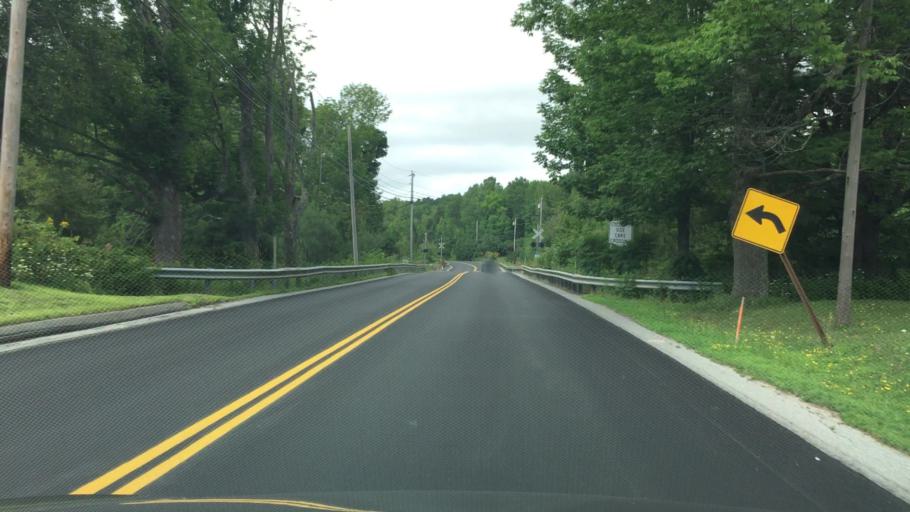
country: US
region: Maine
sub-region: Waldo County
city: Winterport
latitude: 44.6157
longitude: -68.8262
